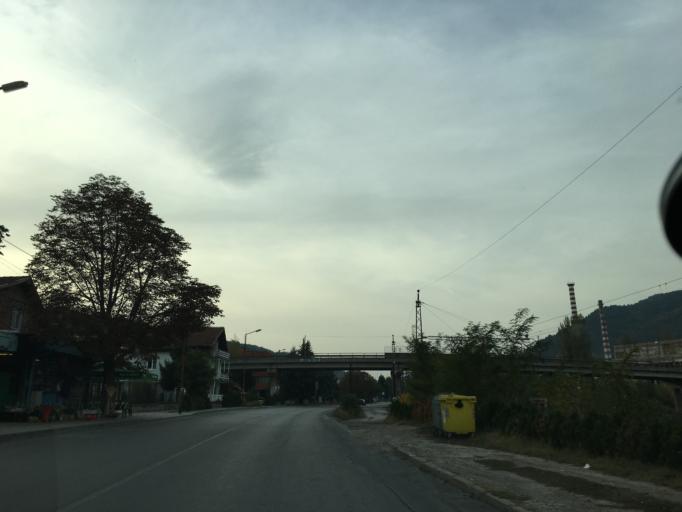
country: BG
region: Pazardzhik
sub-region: Obshtina Belovo
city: Belovo
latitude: 42.2166
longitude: 24.0102
